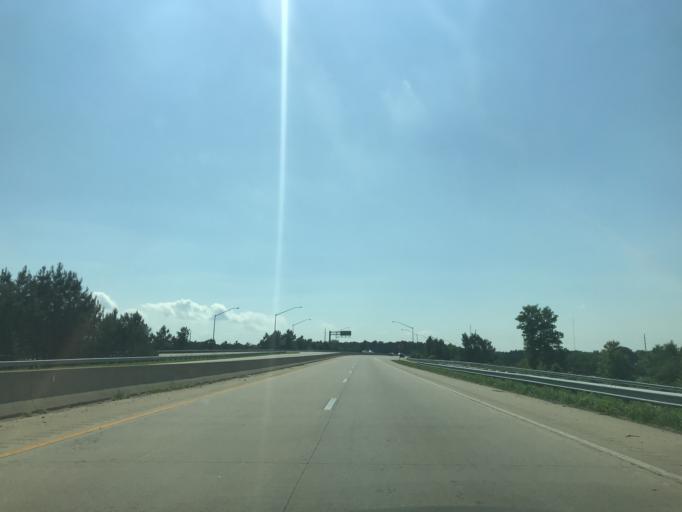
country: US
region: Maryland
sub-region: Wicomico County
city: Salisbury
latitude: 38.4024
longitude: -75.5802
